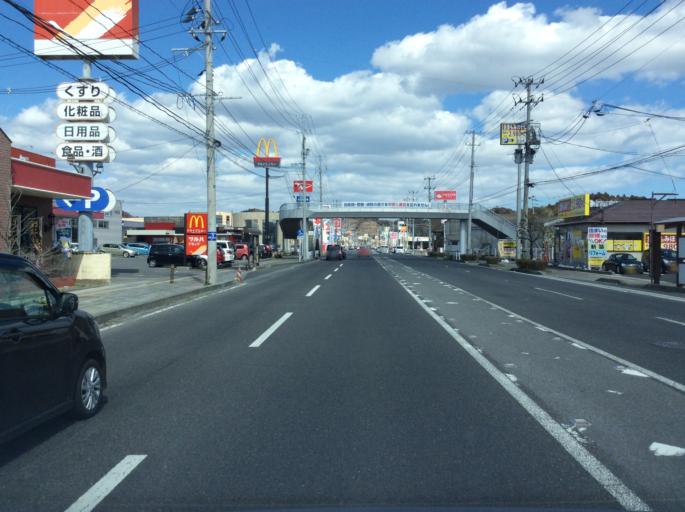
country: JP
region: Fukushima
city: Iwaki
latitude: 36.9592
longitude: 140.9038
